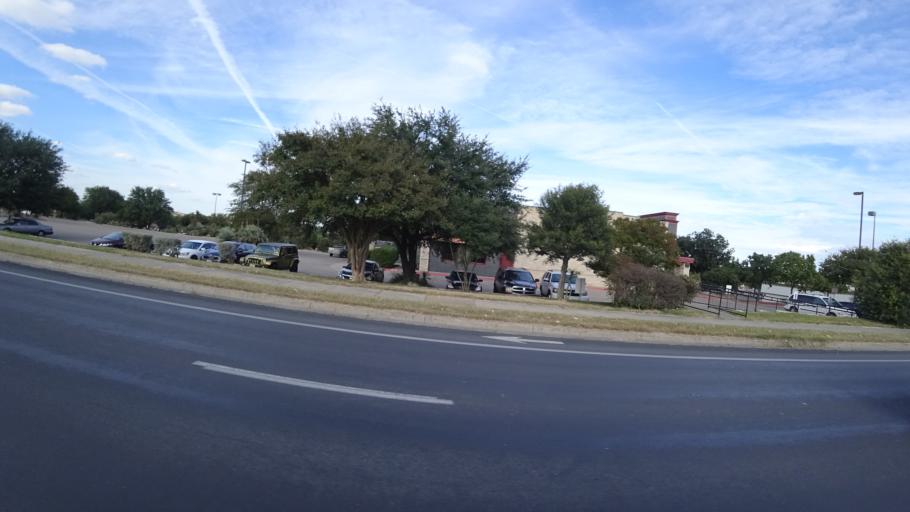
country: US
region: Texas
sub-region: Travis County
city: Onion Creek
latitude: 30.1994
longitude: -97.7654
